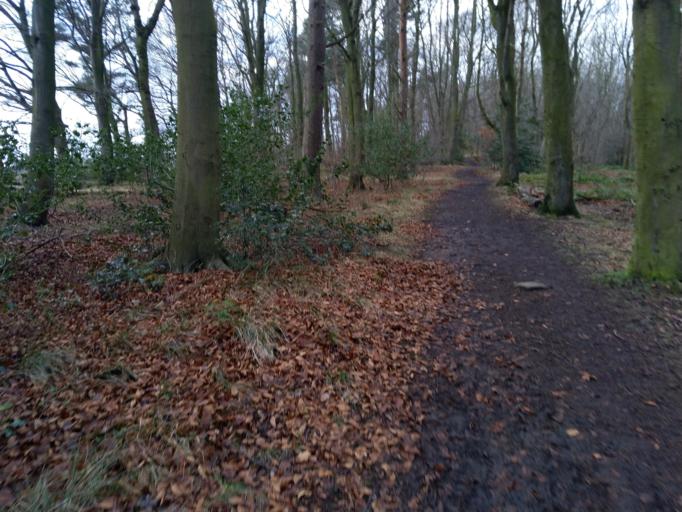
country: GB
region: Scotland
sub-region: Fife
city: Limekilns
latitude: 55.9989
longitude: -3.5150
